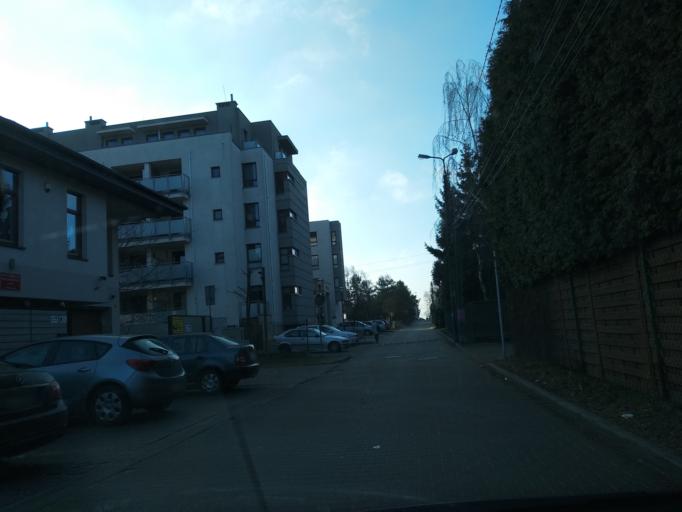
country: PL
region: Masovian Voivodeship
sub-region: Powiat piaseczynski
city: Mysiadlo
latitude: 52.0940
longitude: 21.0121
